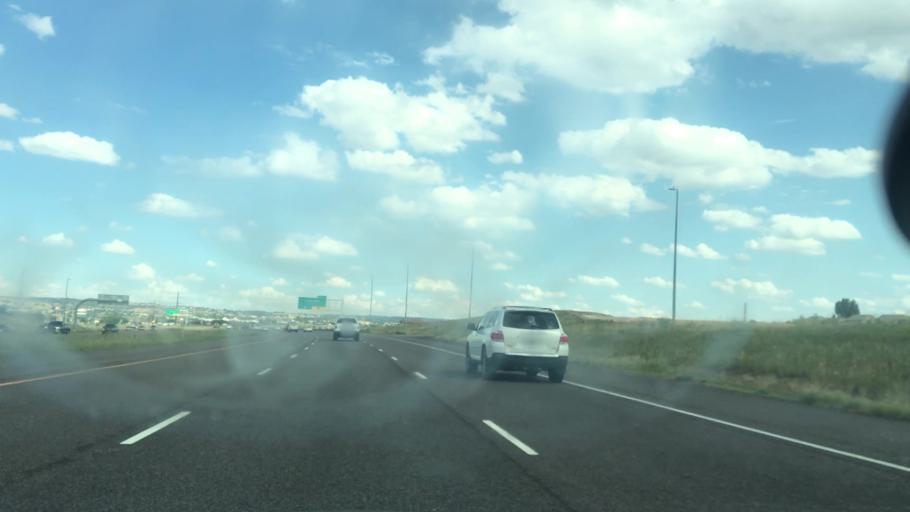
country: US
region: Colorado
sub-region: Douglas County
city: Stonegate
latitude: 39.5513
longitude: -104.8052
